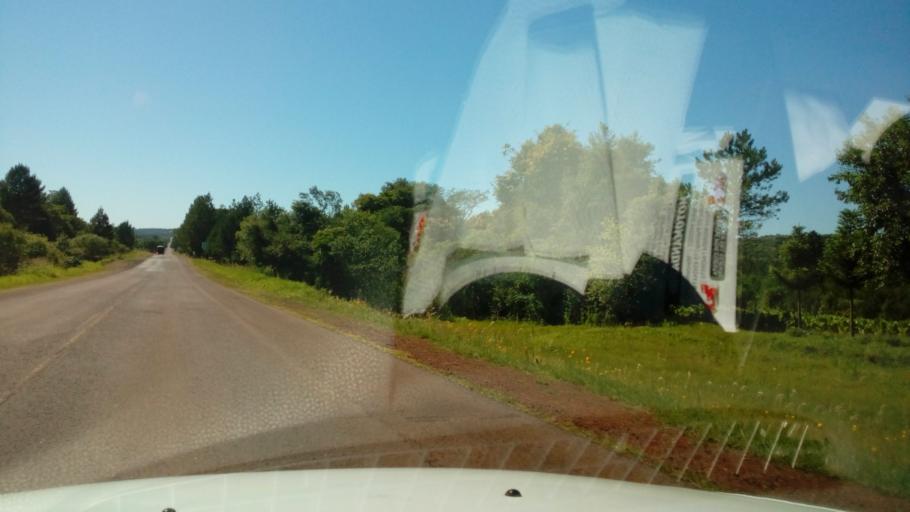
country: AR
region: Misiones
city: Almafuerte
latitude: -27.5619
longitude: -55.4107
